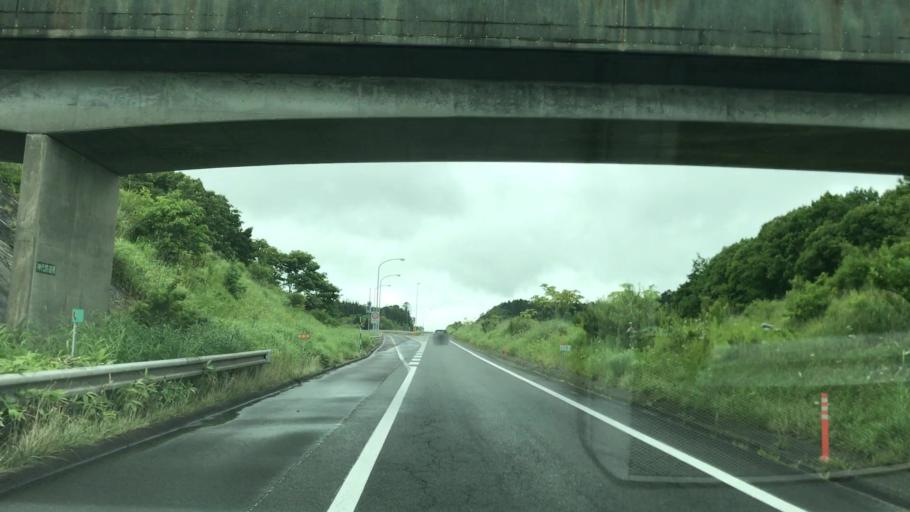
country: JP
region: Hokkaido
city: Muroran
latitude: 42.3842
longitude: 140.9923
